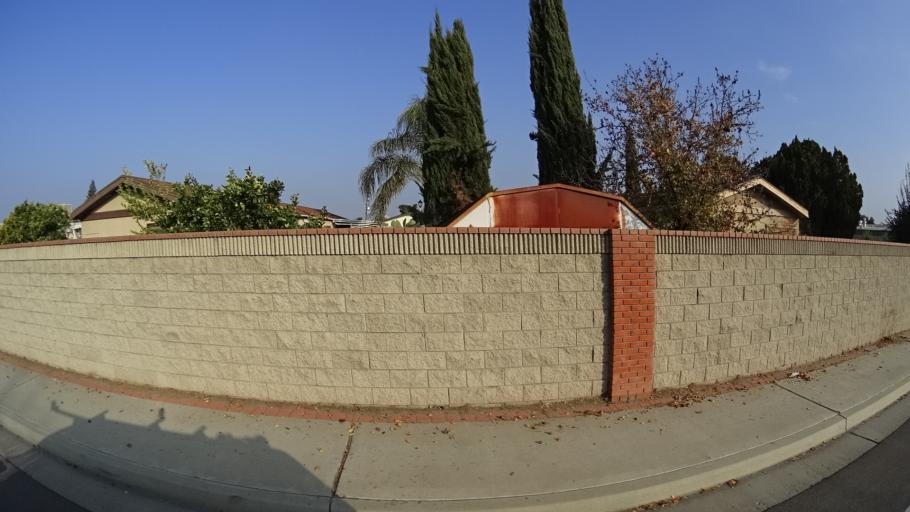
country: US
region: California
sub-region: Kern County
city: Greenfield
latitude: 35.3035
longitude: -119.0599
